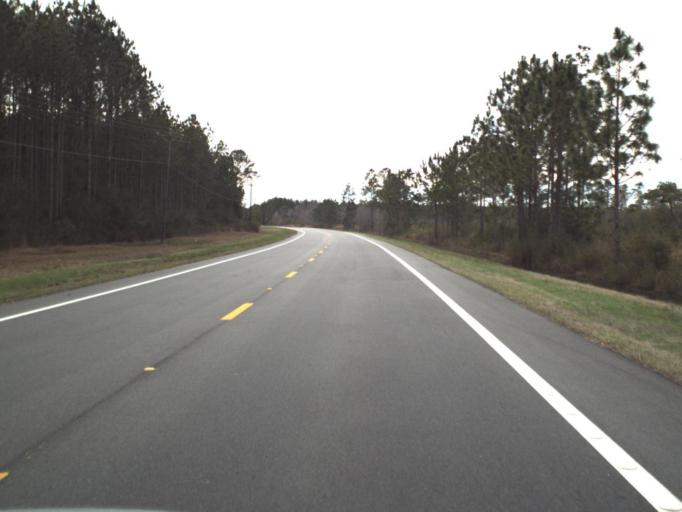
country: US
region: Florida
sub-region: Gulf County
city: Wewahitchka
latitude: 30.1383
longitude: -85.2476
